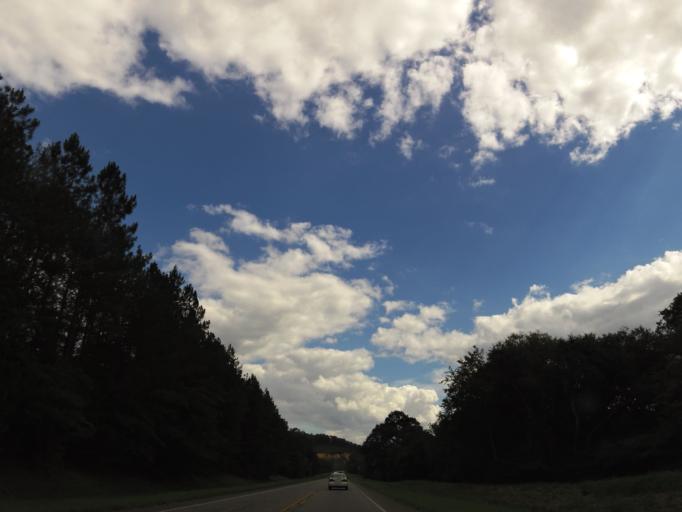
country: US
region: Georgia
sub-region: Walker County
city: Lookout Mountain
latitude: 34.9623
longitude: -85.3375
